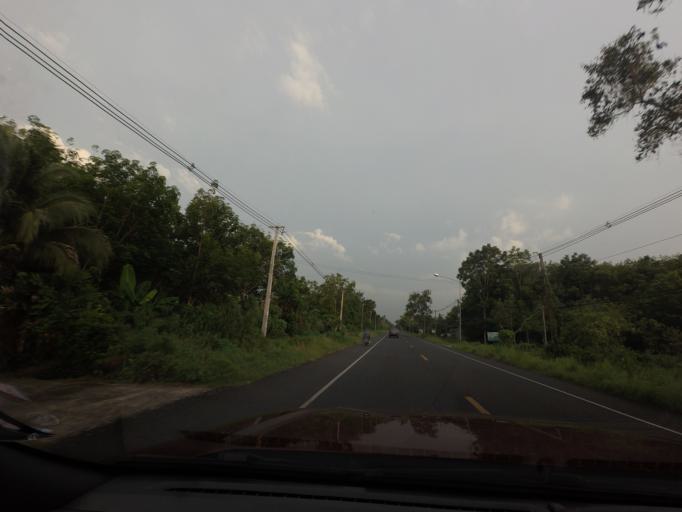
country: TH
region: Pattani
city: Mae Lan
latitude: 6.6140
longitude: 101.1905
